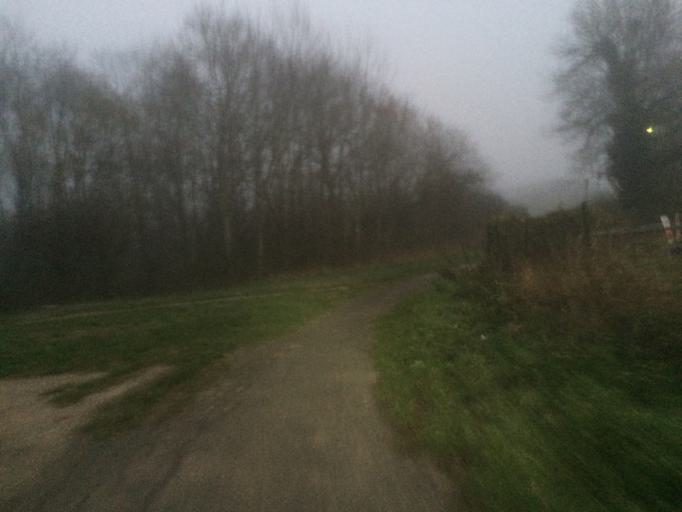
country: FR
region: Ile-de-France
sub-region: Departement de l'Essonne
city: Vauhallan
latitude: 48.7485
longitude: 2.1973
